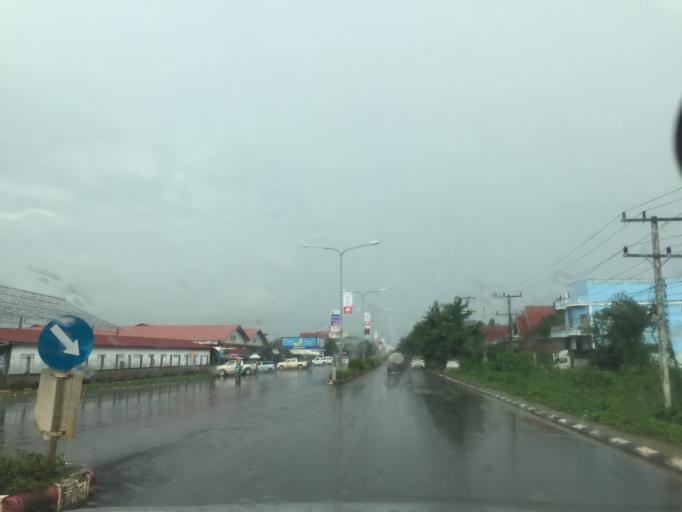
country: LA
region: Attapu
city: Attapu
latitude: 14.8172
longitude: 106.8178
